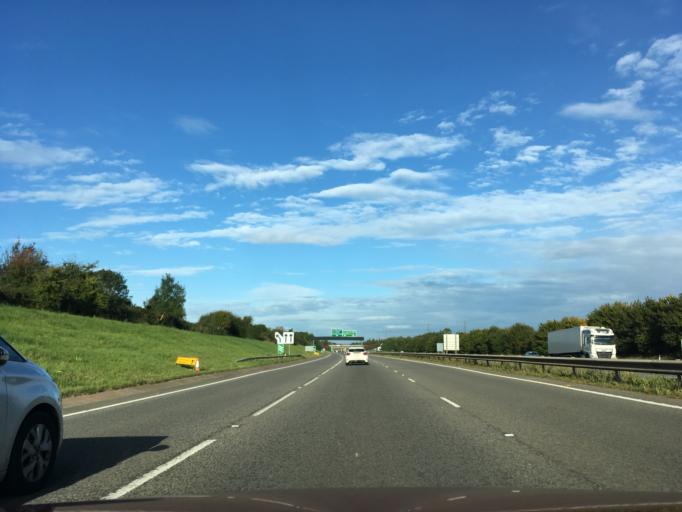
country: GB
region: England
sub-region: Gloucestershire
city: Churchdown
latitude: 51.8550
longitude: -2.1583
